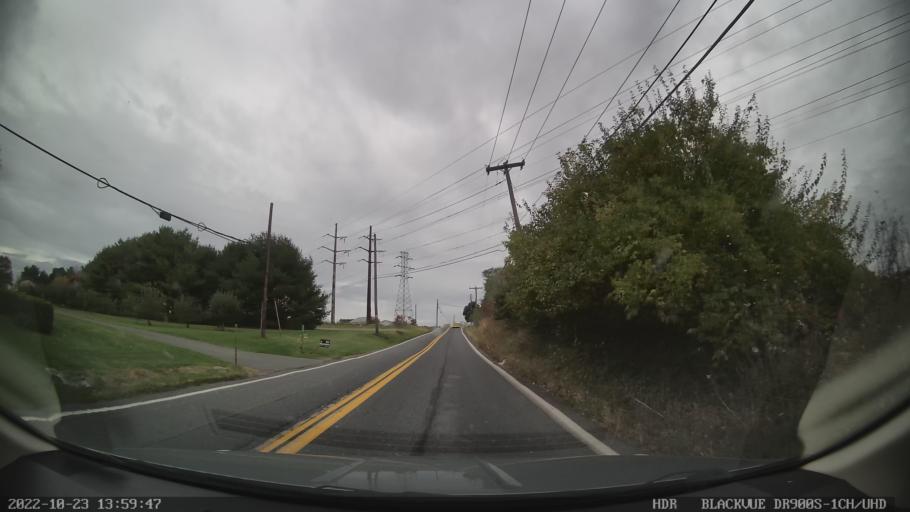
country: US
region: Pennsylvania
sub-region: Northampton County
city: Northampton
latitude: 40.7098
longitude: -75.4788
